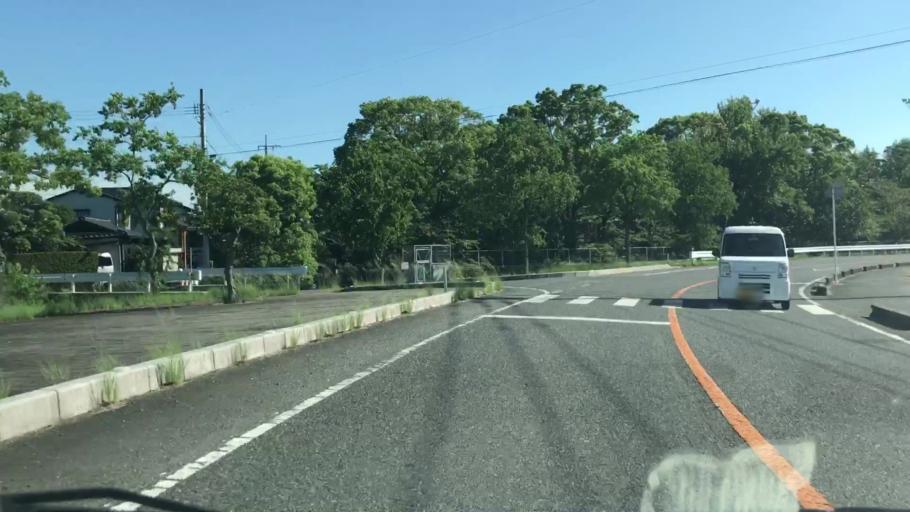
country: JP
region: Saga Prefecture
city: Okawa
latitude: 33.2279
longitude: 130.3559
